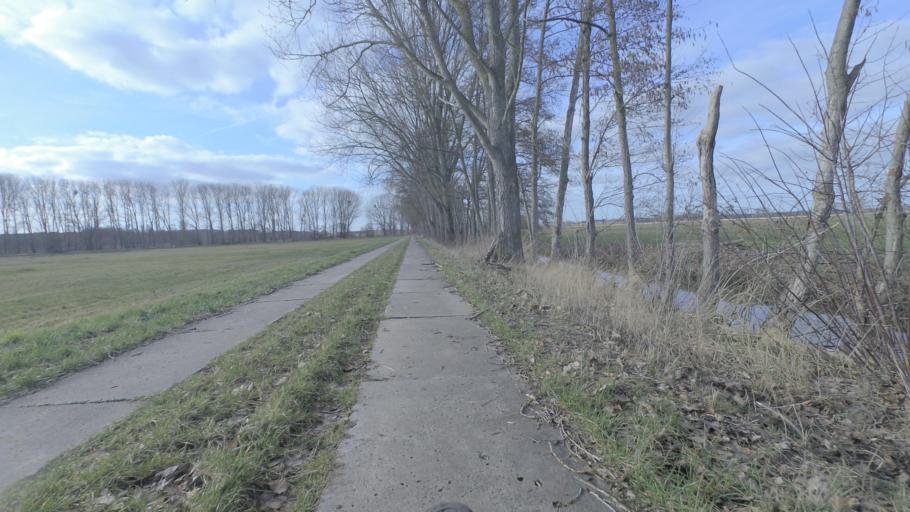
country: DE
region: Brandenburg
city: Trebbin
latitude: 52.2244
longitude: 13.2587
